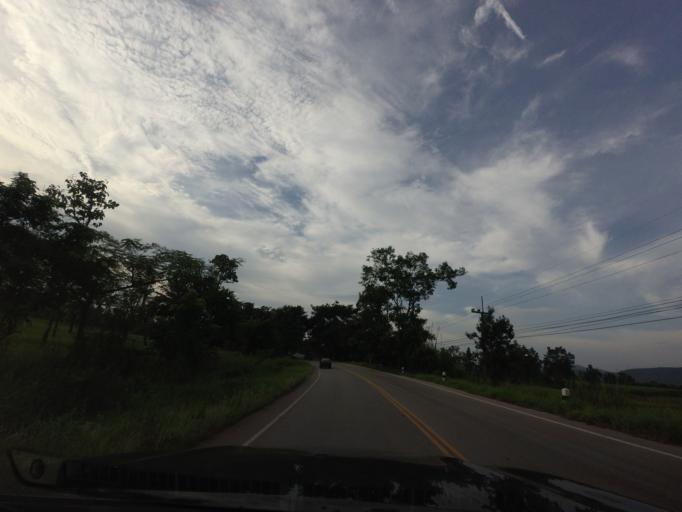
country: TH
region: Changwat Udon Thani
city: Nam Som
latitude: 17.8352
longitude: 102.2606
